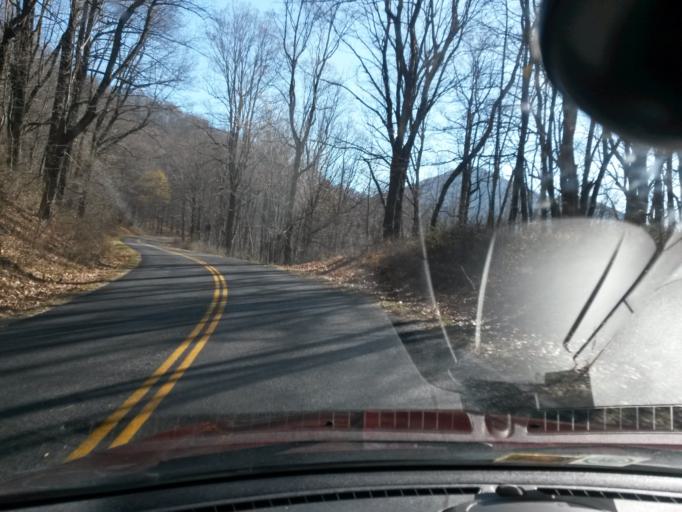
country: US
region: Virginia
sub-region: Botetourt County
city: Buchanan
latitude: 37.4491
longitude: -79.6221
